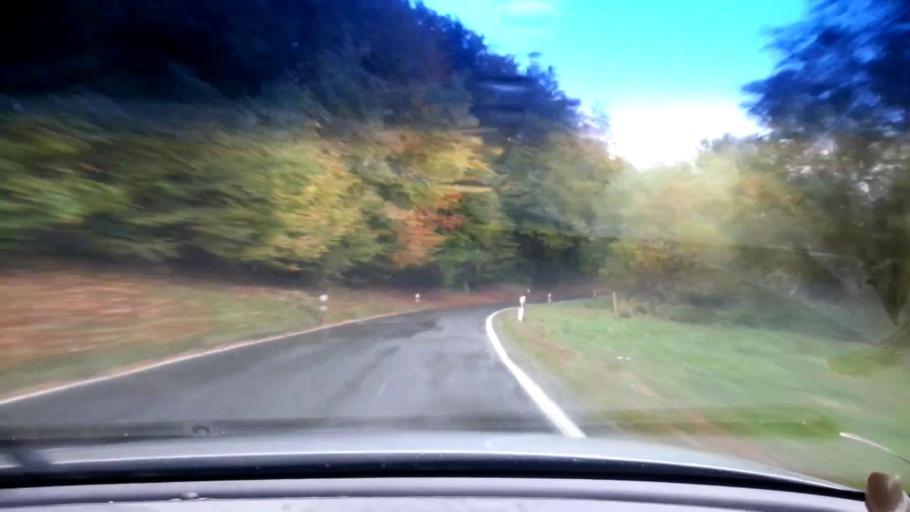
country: DE
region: Bavaria
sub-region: Upper Franconia
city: Stadelhofen
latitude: 50.0319
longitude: 11.2013
